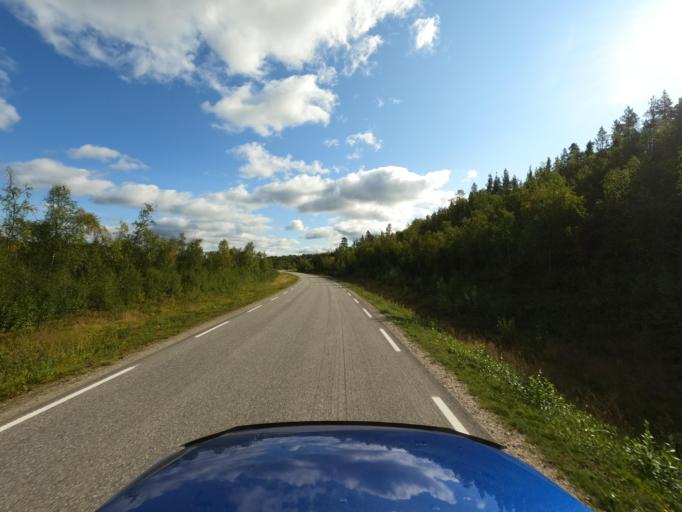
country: NO
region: Finnmark Fylke
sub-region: Karasjok
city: Karasjohka
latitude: 69.4490
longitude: 25.5892
